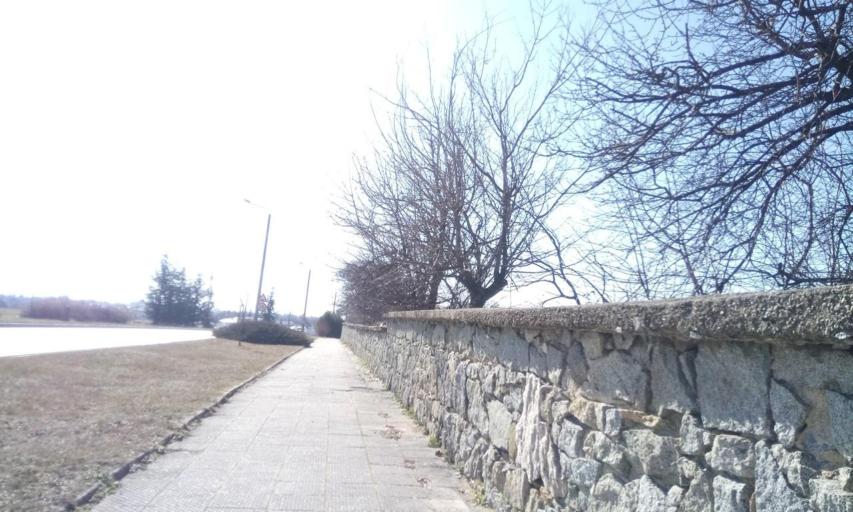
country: BG
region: Plovdiv
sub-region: Obshtina Khisarya
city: Khisarya
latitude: 42.5141
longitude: 24.7179
